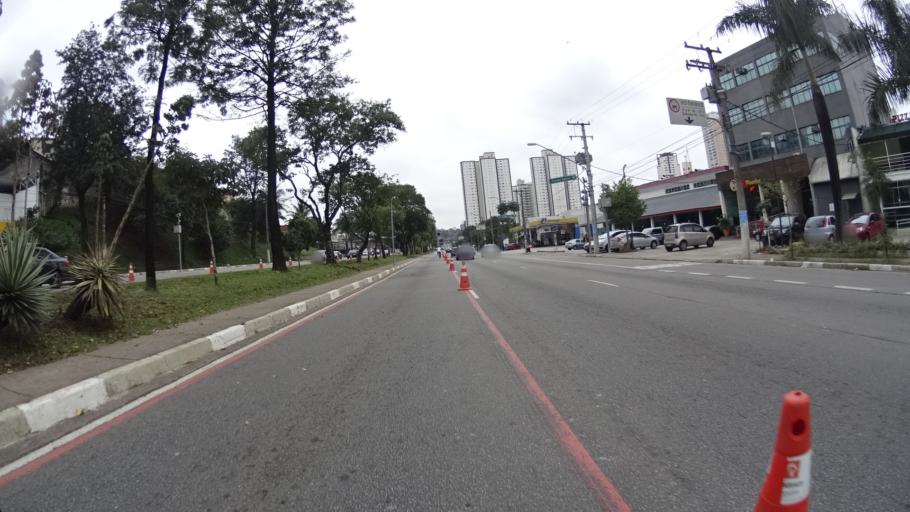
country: BR
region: Sao Paulo
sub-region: Sao Paulo
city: Sao Paulo
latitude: -23.4910
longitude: -46.6106
